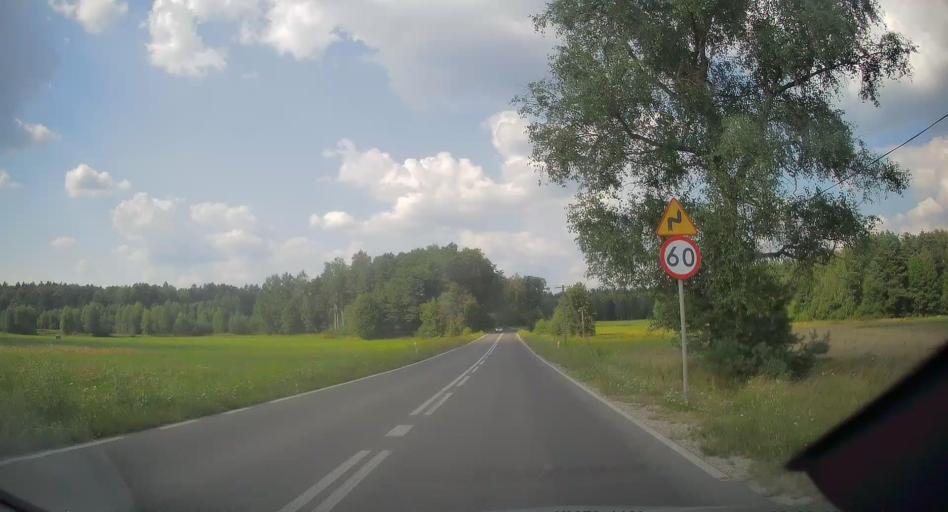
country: PL
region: Swietokrzyskie
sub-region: Powiat jedrzejowski
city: Malogoszcz
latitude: 50.8793
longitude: 20.2681
